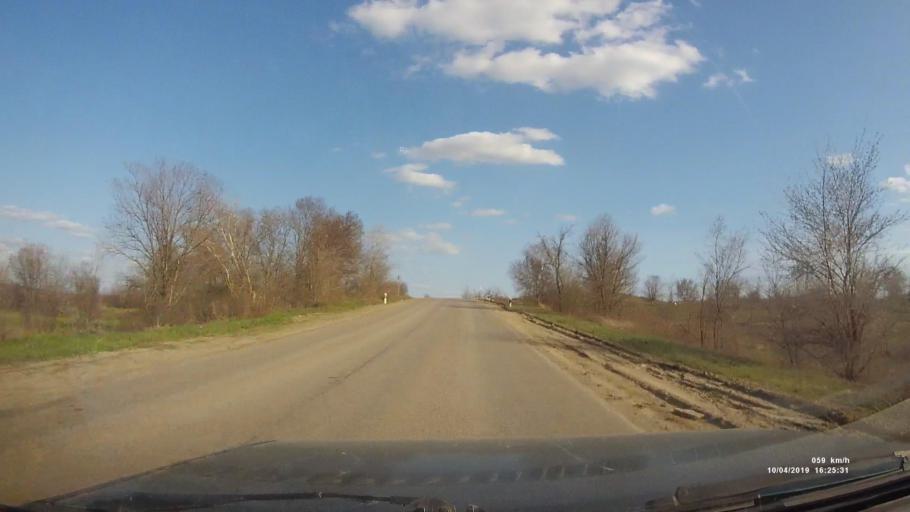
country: RU
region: Rostov
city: Staraya Stanitsa
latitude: 48.2924
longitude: 40.3242
